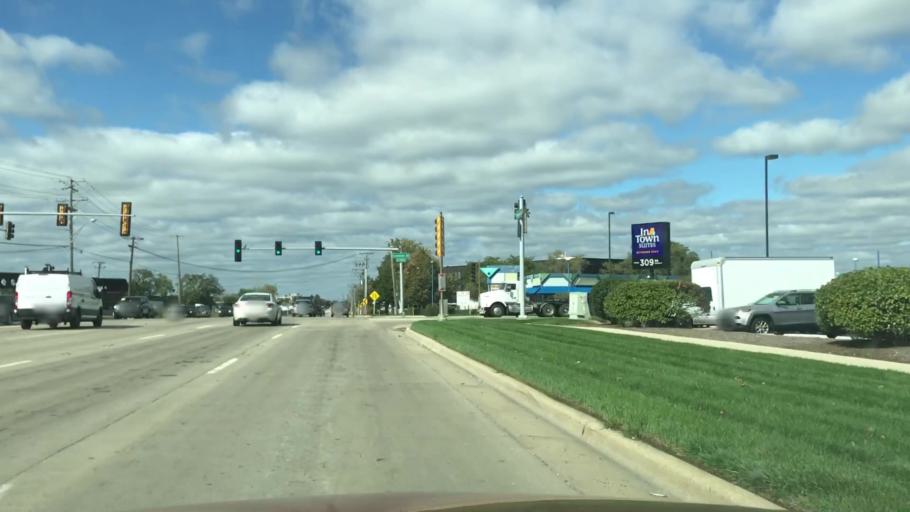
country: US
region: Illinois
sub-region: Cook County
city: Elk Grove Village
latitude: 42.0101
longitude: -87.9438
